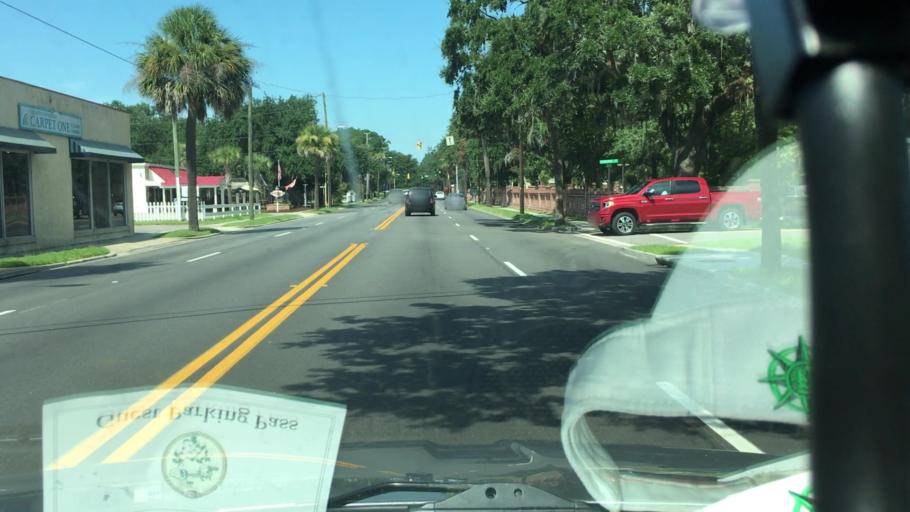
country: US
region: South Carolina
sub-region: Beaufort County
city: Beaufort
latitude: 32.4397
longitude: -80.6774
